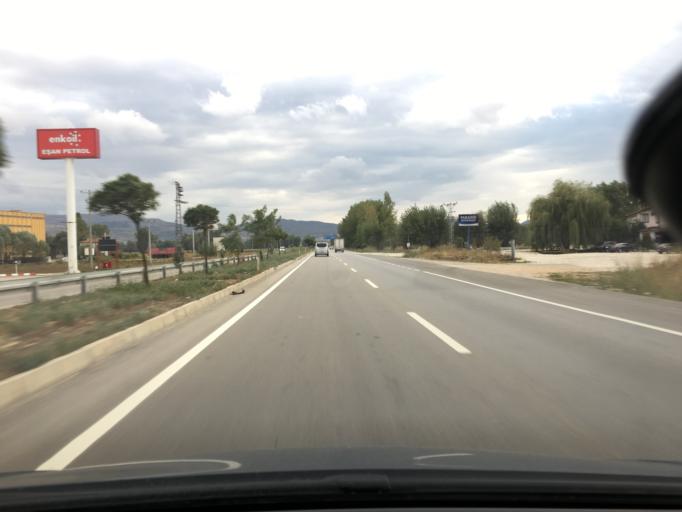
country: TR
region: Afyonkarahisar
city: Sincanli
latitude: 38.7577
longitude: 30.3618
